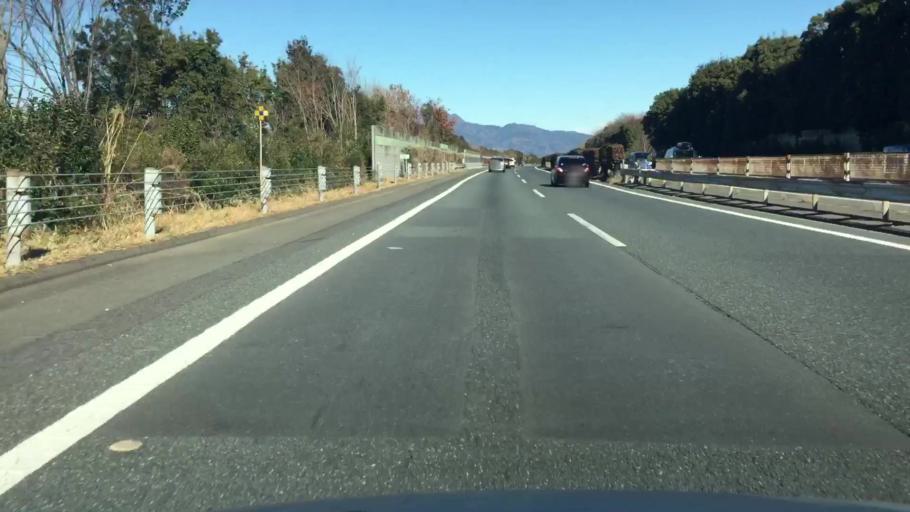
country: JP
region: Gunma
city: Kanekomachi
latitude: 36.4365
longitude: 139.0143
